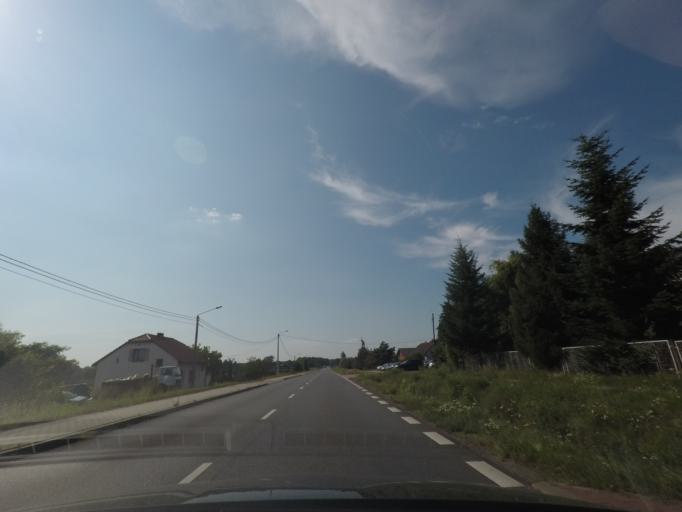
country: PL
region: Silesian Voivodeship
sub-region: Powiat pszczynski
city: Radostowice
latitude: 50.0104
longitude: 18.8622
